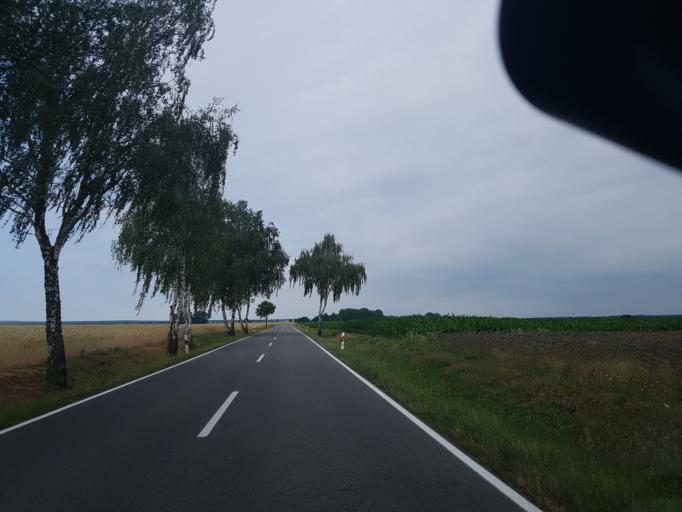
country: DE
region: Brandenburg
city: Schonewalde
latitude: 51.6949
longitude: 13.5582
